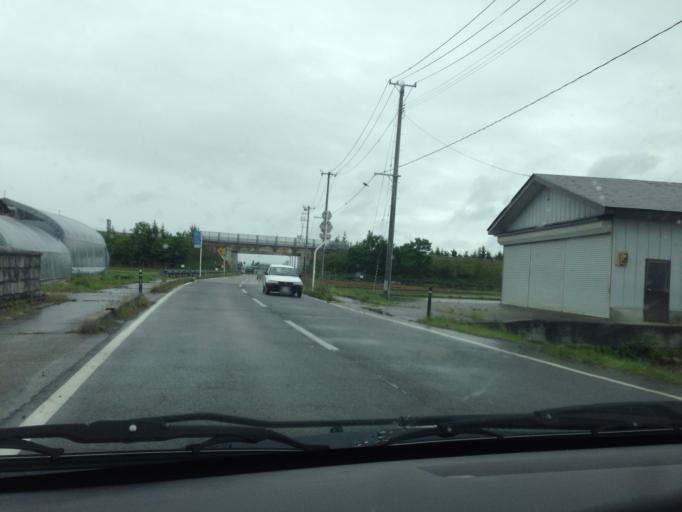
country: JP
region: Fukushima
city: Kitakata
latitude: 37.5287
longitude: 139.8341
